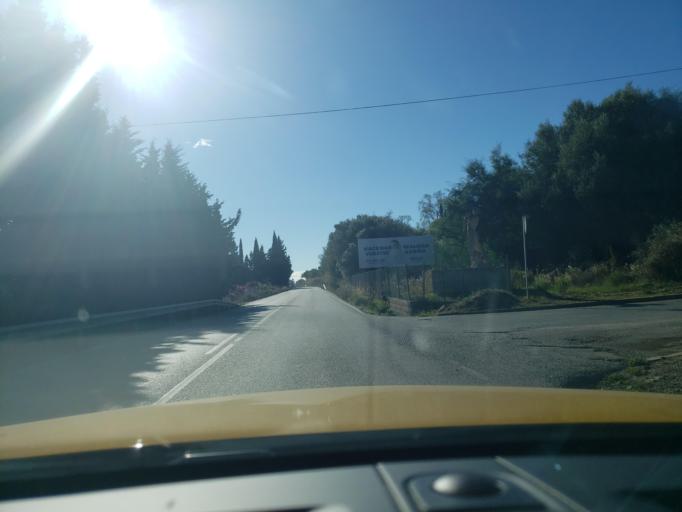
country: ES
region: Andalusia
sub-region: Provincia de Malaga
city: Benahavis
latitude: 36.4799
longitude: -5.0142
